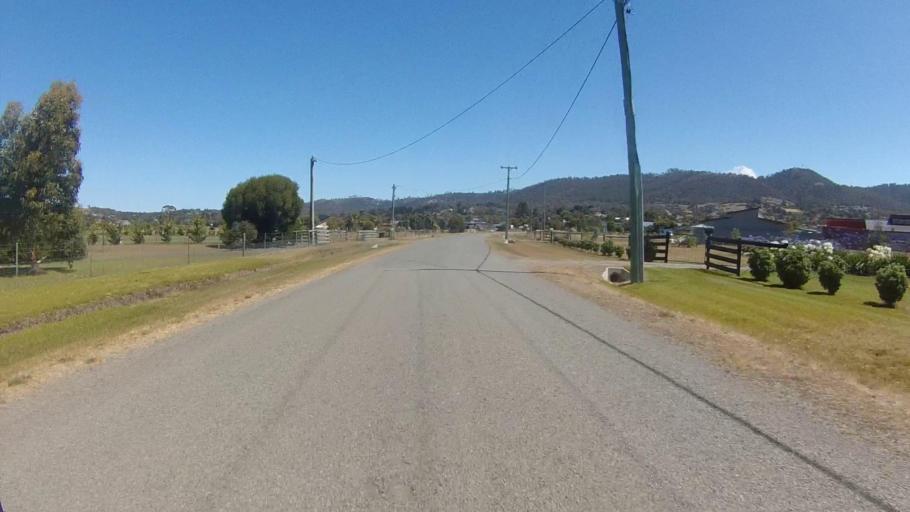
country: AU
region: Tasmania
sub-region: Clarence
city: Seven Mile Beach
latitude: -42.8517
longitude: 147.4913
